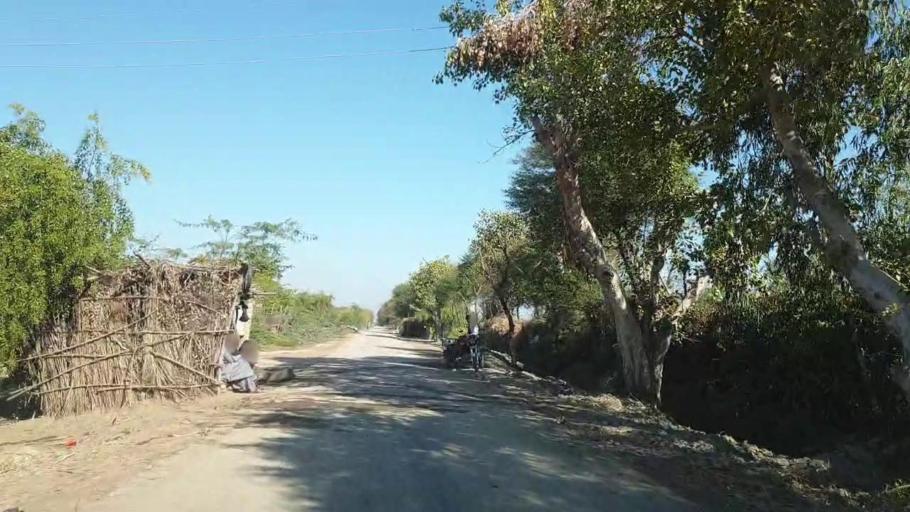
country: PK
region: Sindh
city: Mirpur Khas
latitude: 25.6114
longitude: 69.0242
